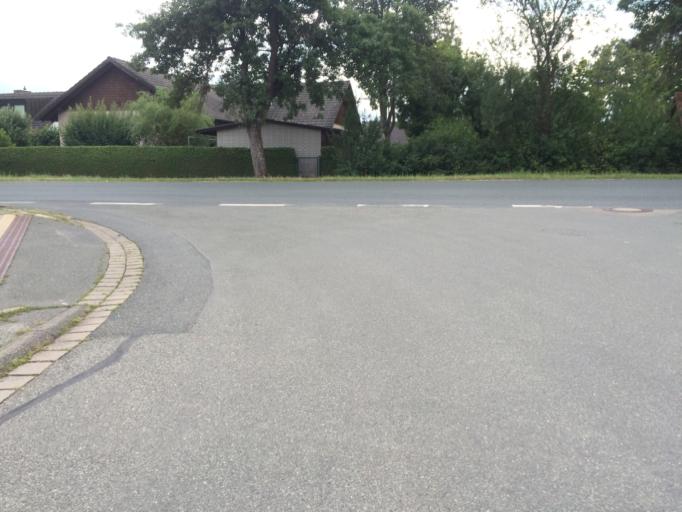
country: DE
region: Bavaria
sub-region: Regierungsbezirk Mittelfranken
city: Wilhermsdorf
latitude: 49.4802
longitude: 10.7058
